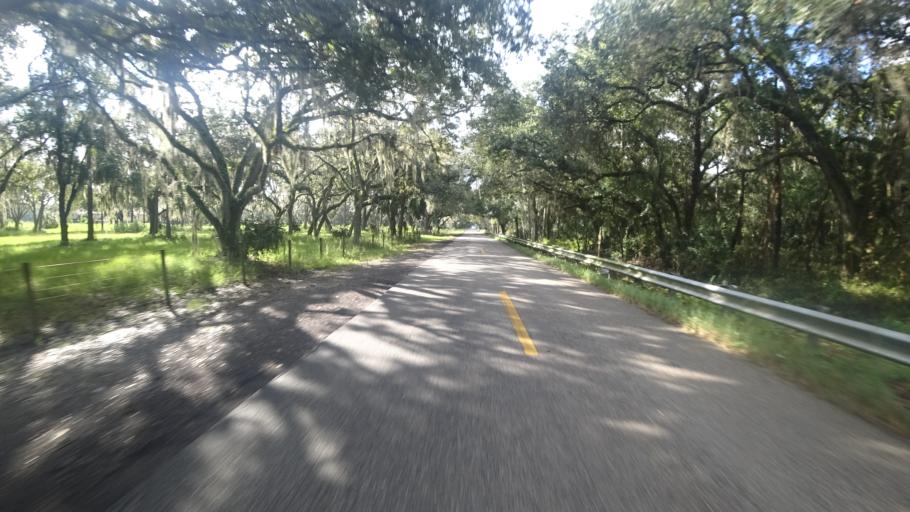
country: US
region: Florida
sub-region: Manatee County
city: Ellenton
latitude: 27.5859
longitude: -82.4091
